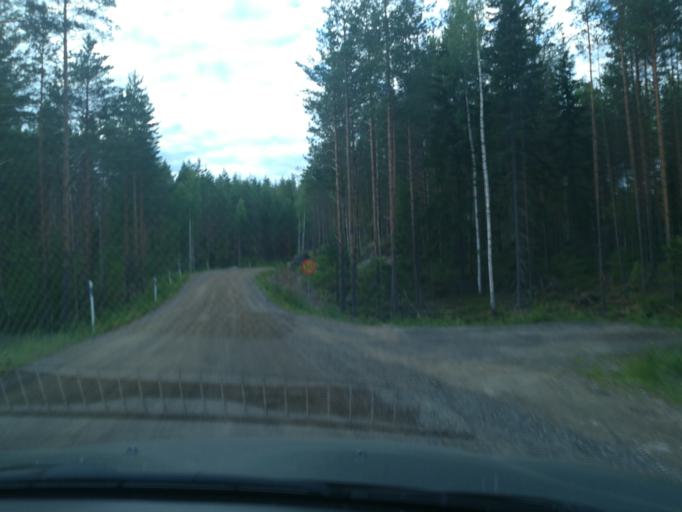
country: FI
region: Southern Savonia
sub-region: Mikkeli
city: Puumala
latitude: 61.5781
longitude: 28.1629
